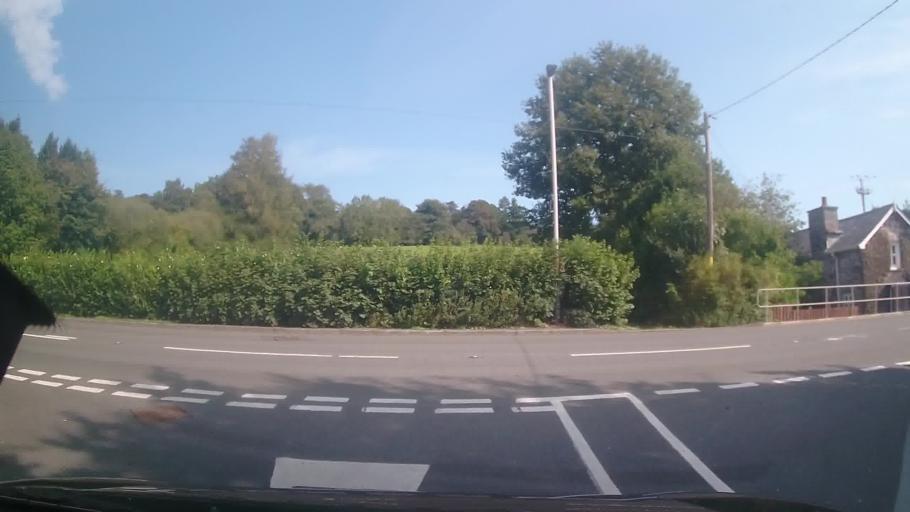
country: GB
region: Wales
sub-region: Sir Powys
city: Rhayader
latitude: 52.3054
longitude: -3.5142
